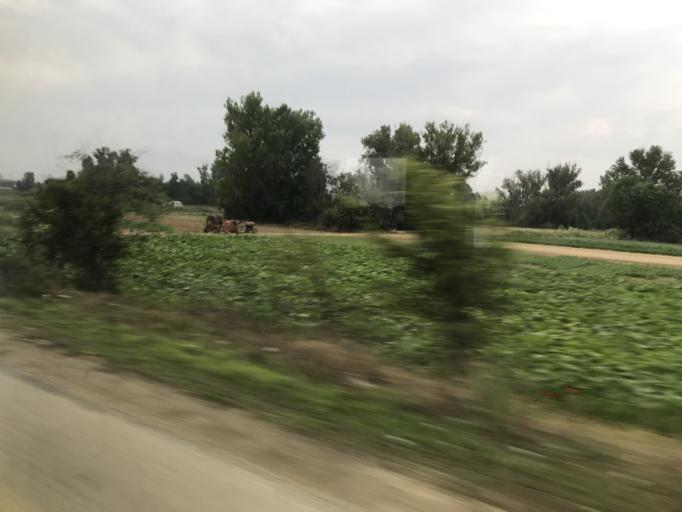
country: GR
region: East Macedonia and Thrace
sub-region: Nomos Rodopis
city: Arisvi
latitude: 41.0612
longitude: 25.5974
